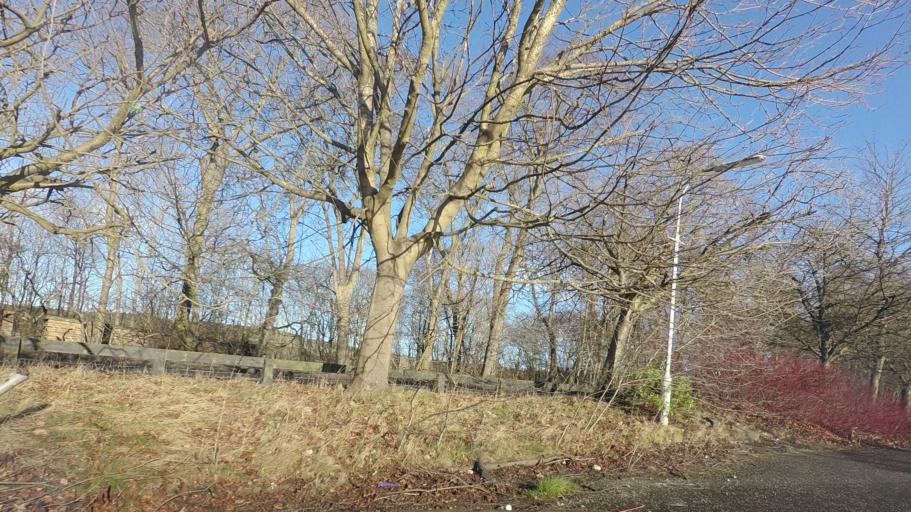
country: GB
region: Scotland
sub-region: Fife
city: Crossgates
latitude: 56.0439
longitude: -3.3555
